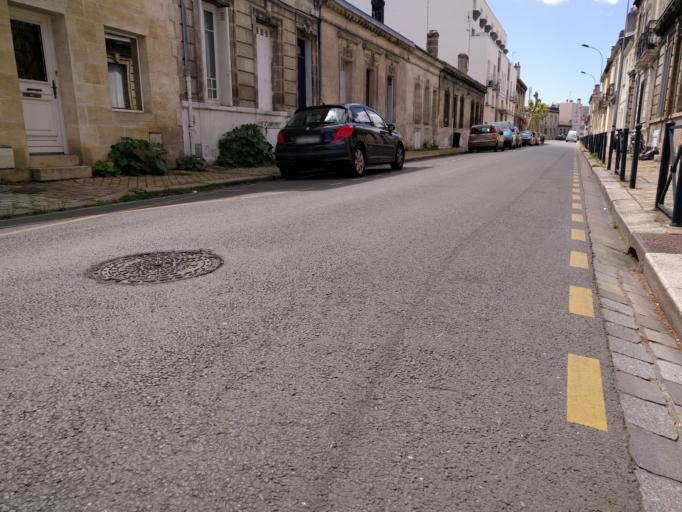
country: FR
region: Aquitaine
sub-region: Departement de la Gironde
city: Bordeaux
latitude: 44.8232
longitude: -0.5760
